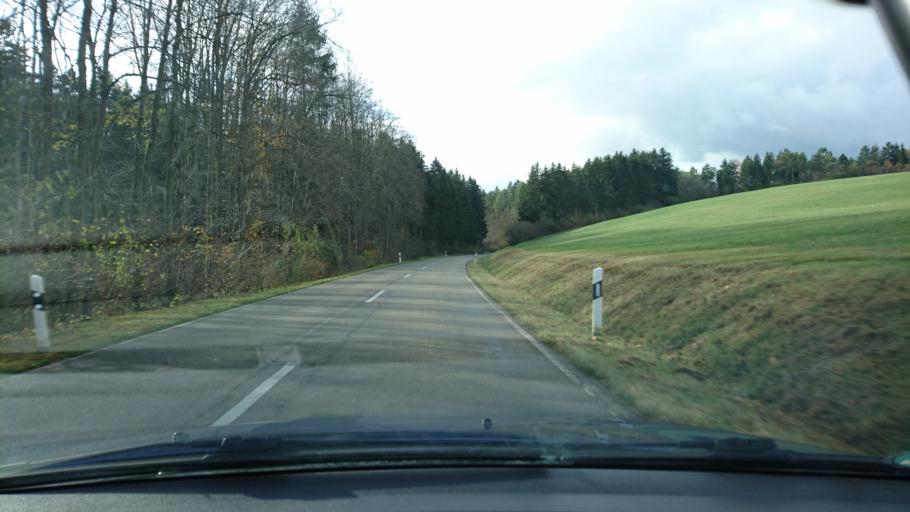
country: DE
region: Baden-Wuerttemberg
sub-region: Regierungsbezirk Stuttgart
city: Neresheim
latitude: 48.7651
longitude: 10.3528
